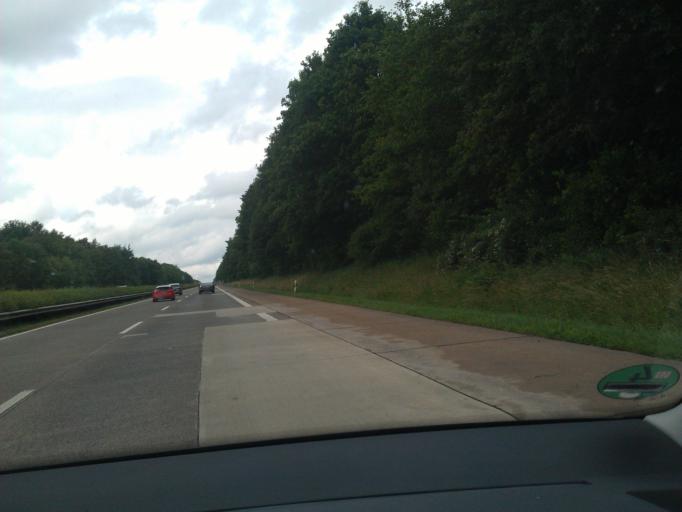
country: DE
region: Rheinland-Pfalz
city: Fohren
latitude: 49.8380
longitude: 6.7709
